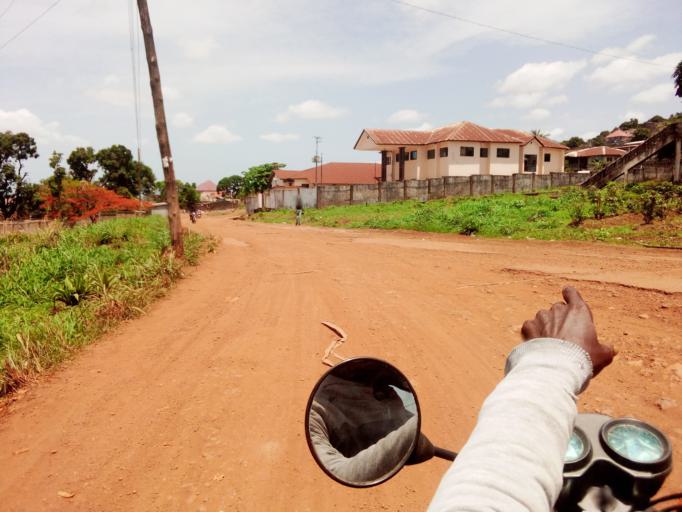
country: SL
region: Western Area
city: Waterloo
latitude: 8.3369
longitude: -13.0750
